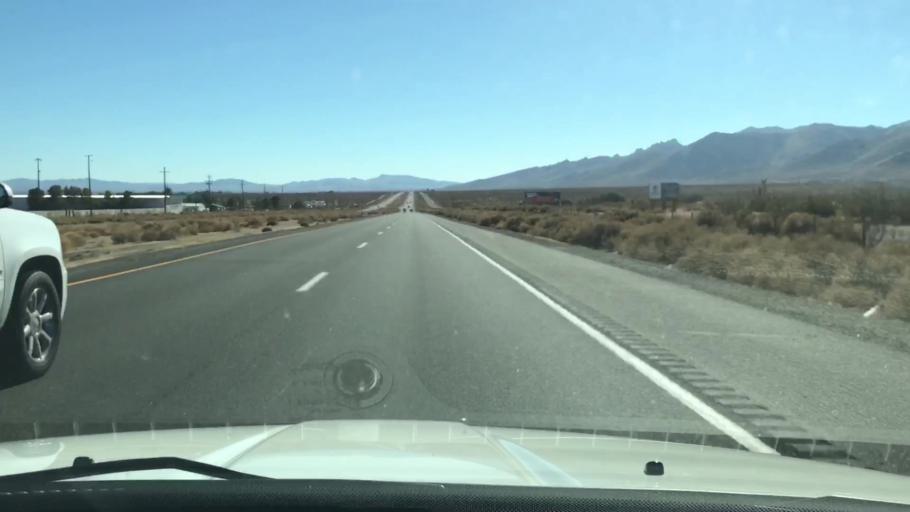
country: US
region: California
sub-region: Kern County
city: Inyokern
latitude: 35.8064
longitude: -117.8734
